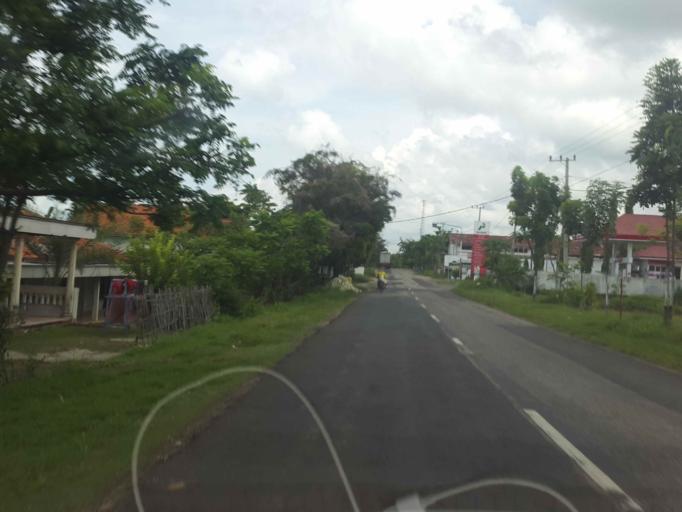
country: ID
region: East Java
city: Pesisir
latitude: -7.1164
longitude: 113.7586
